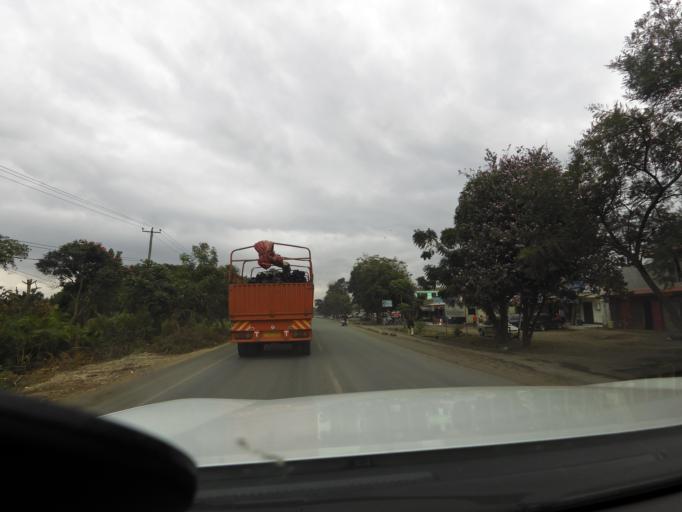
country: TZ
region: Arusha
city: Arusha
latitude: -3.3625
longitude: 36.6798
